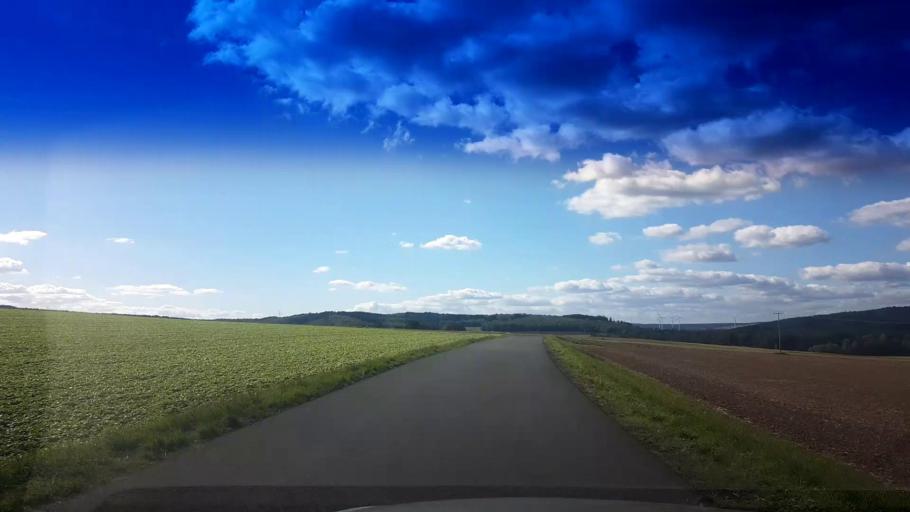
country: DE
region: Bavaria
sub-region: Upper Franconia
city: Arzberg
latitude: 50.0240
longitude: 12.2292
